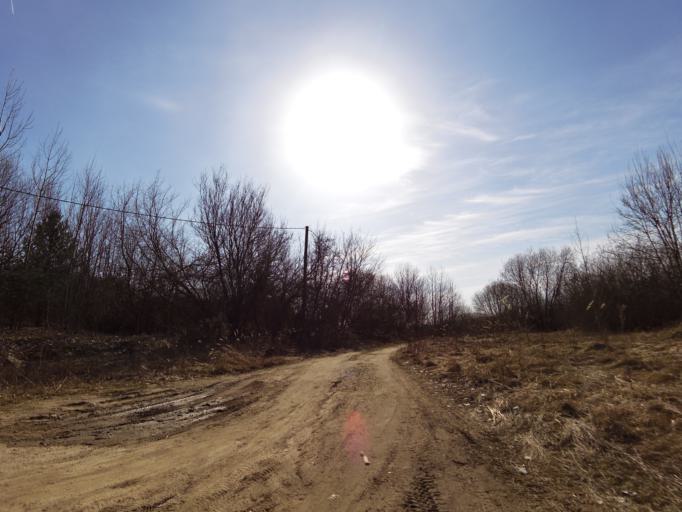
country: LT
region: Vilnius County
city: Seskine
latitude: 54.7070
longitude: 25.2584
